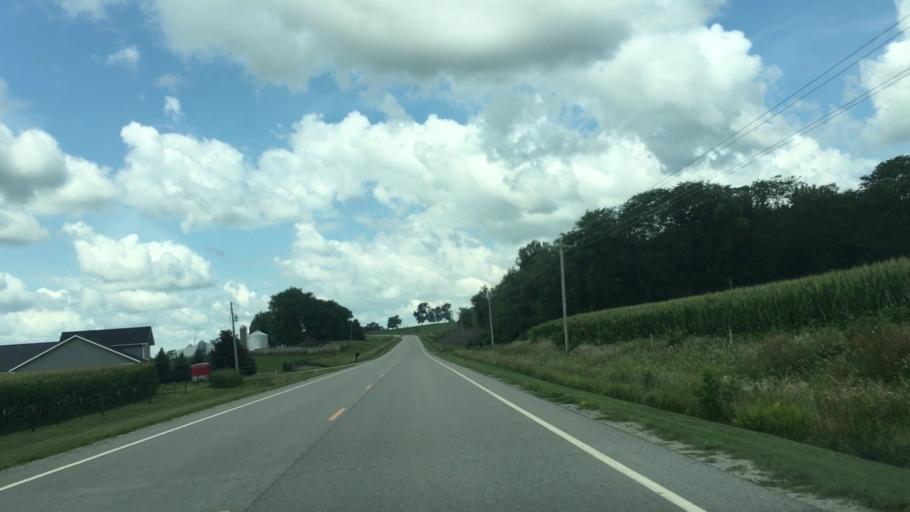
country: US
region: Iowa
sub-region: Linn County
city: Mount Vernon
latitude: 41.8420
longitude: -91.4105
